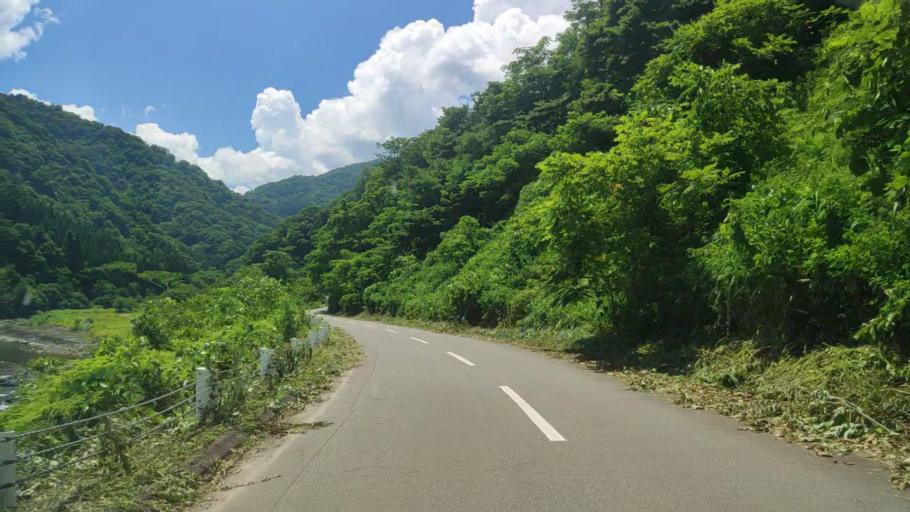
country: JP
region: Fukui
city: Ono
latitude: 35.8749
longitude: 136.4956
